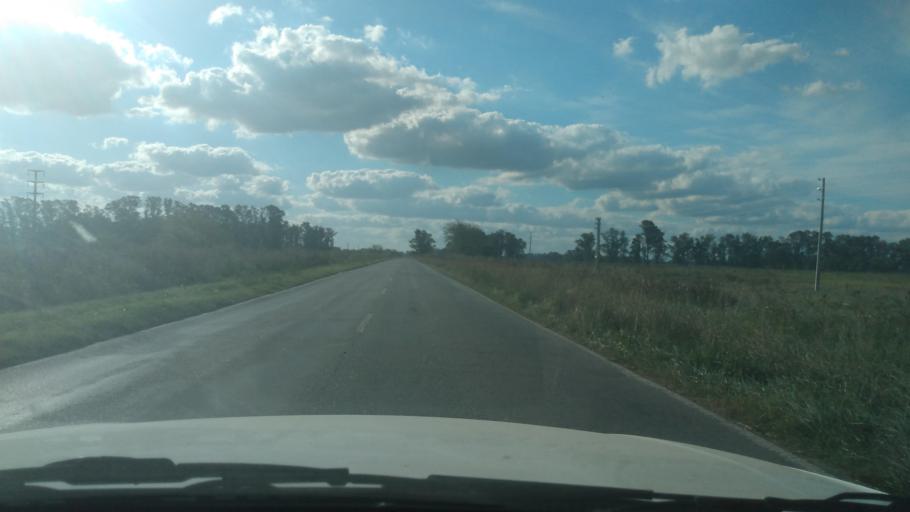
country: AR
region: Buenos Aires
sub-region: Partido de Mercedes
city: Mercedes
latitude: -34.7460
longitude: -59.3829
